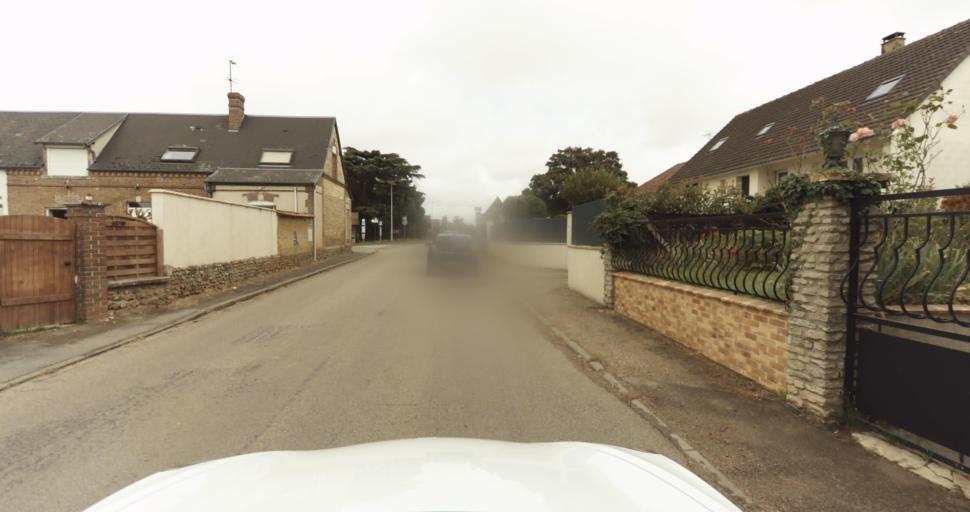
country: FR
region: Haute-Normandie
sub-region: Departement de l'Eure
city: Aviron
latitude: 49.0534
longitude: 1.0865
